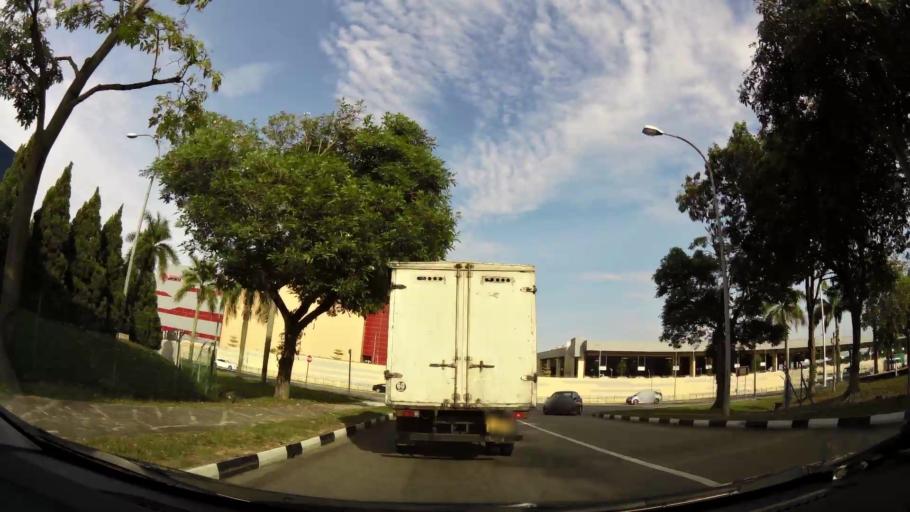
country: MY
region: Johor
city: Johor Bahru
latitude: 1.3367
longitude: 103.6451
